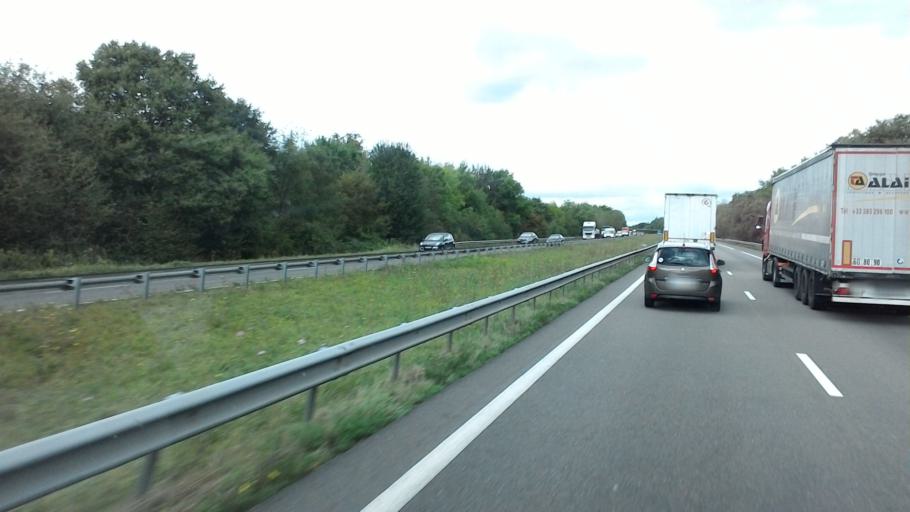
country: FR
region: Lorraine
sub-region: Departement de Meurthe-et-Moselle
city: Pont-a-Mousson
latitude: 48.9072
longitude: 6.1084
